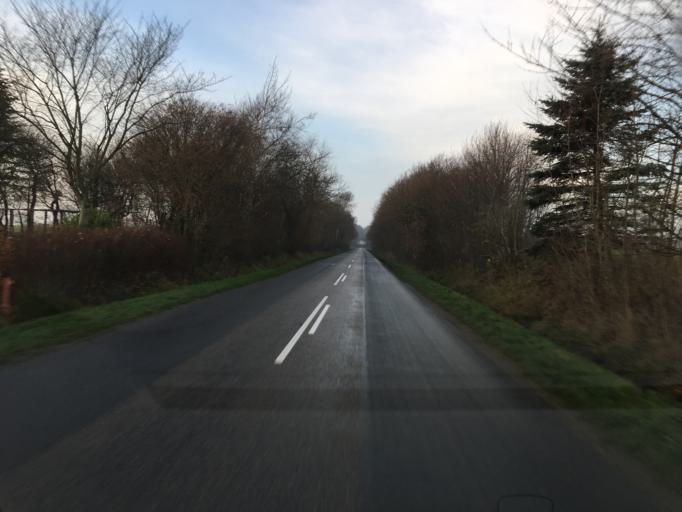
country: DK
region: South Denmark
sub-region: Tonder Kommune
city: Toftlund
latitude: 55.1381
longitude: 9.0585
